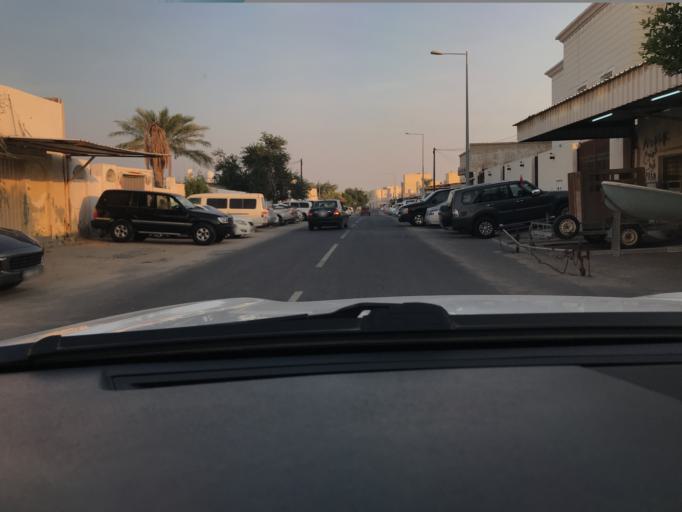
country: QA
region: Baladiyat ad Dawhah
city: Doha
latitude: 25.2528
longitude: 51.5038
